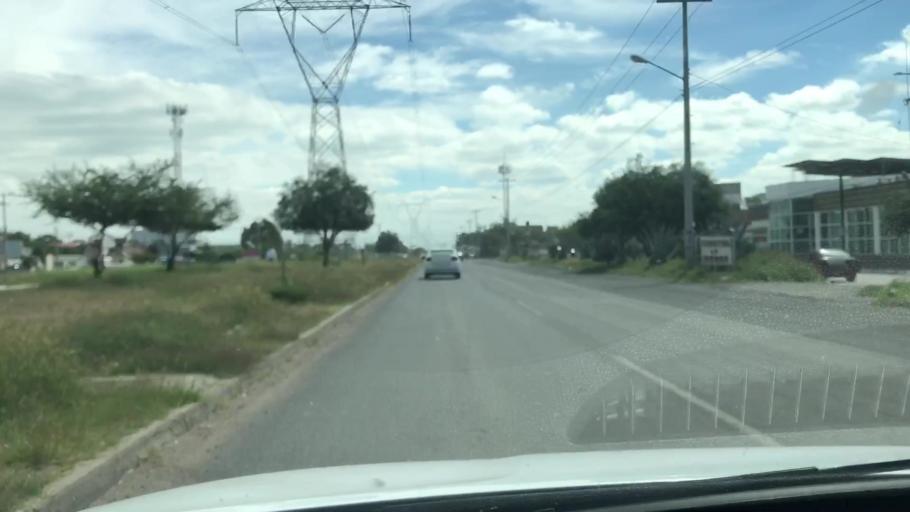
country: MX
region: Guanajuato
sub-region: Celaya
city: La Trinidad
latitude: 20.5488
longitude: -100.7863
